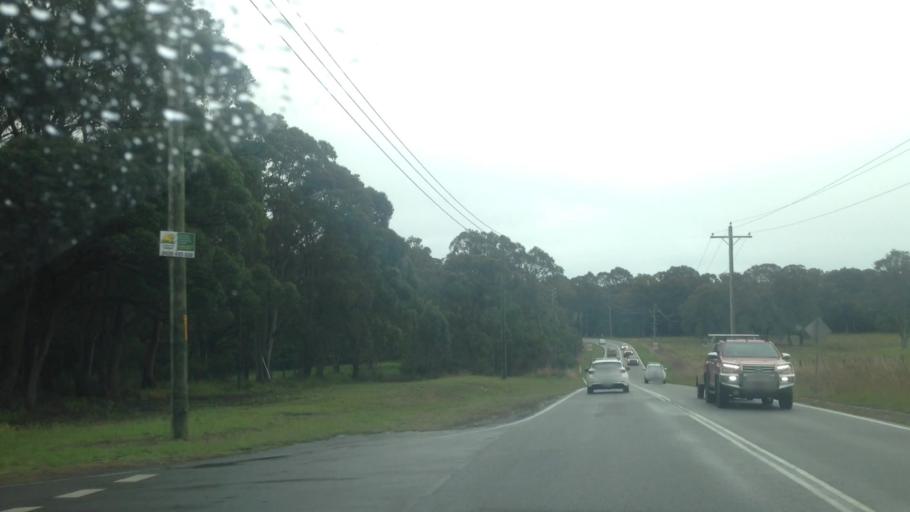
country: AU
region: New South Wales
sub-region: Wyong Shire
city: Charmhaven
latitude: -33.1667
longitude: 151.4764
